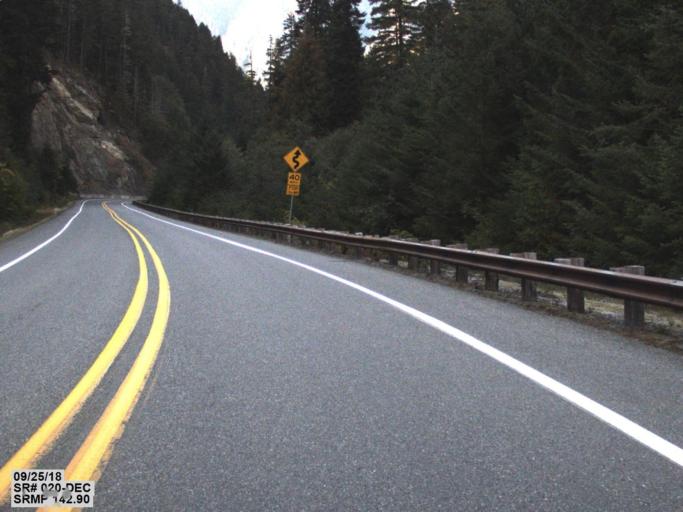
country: US
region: Washington
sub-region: Snohomish County
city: Darrington
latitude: 48.6909
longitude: -120.8911
